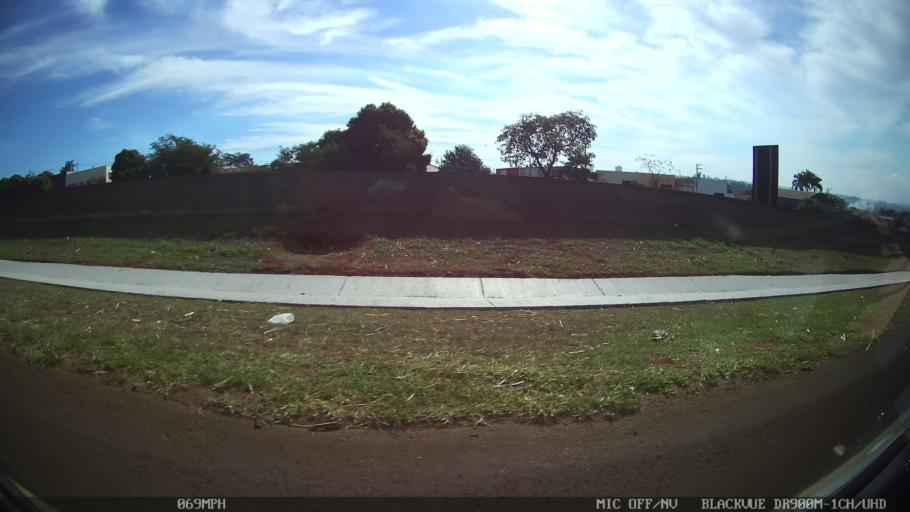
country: BR
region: Sao Paulo
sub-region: Araraquara
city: Araraquara
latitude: -21.8083
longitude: -48.1526
